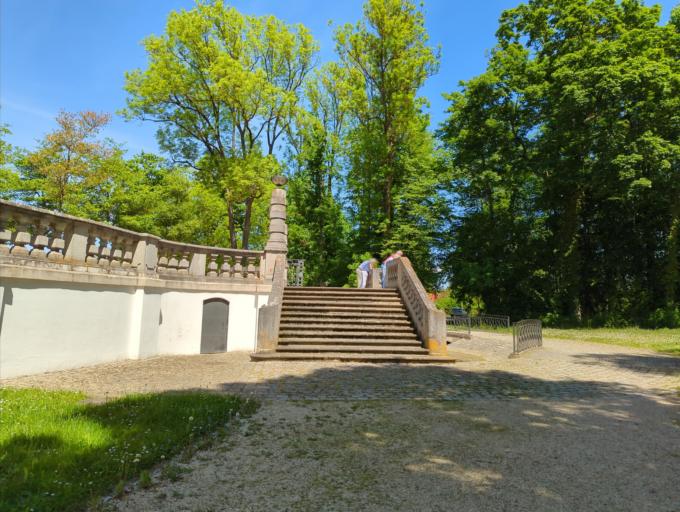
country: DE
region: Bavaria
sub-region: Upper Palatinate
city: Alteglofsheim
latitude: 48.9184
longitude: 12.2052
